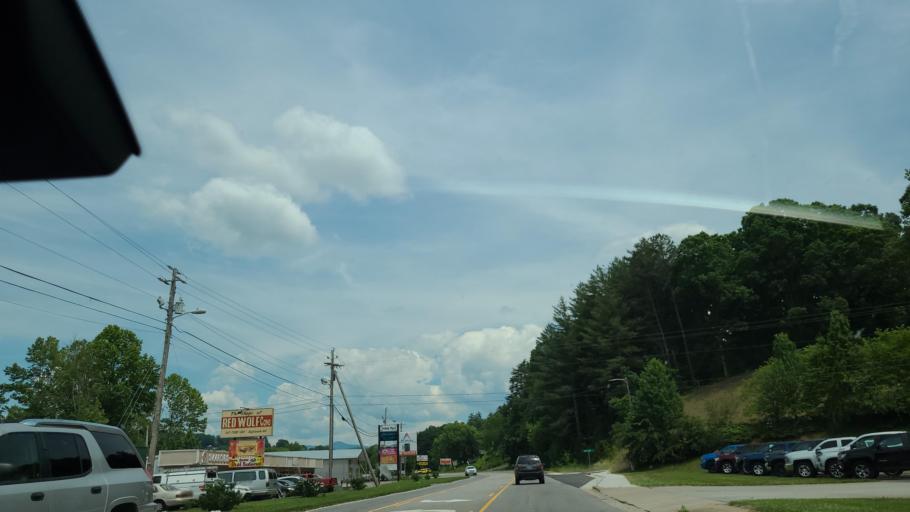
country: US
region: North Carolina
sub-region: Macon County
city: Franklin
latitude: 35.1797
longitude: -83.3671
